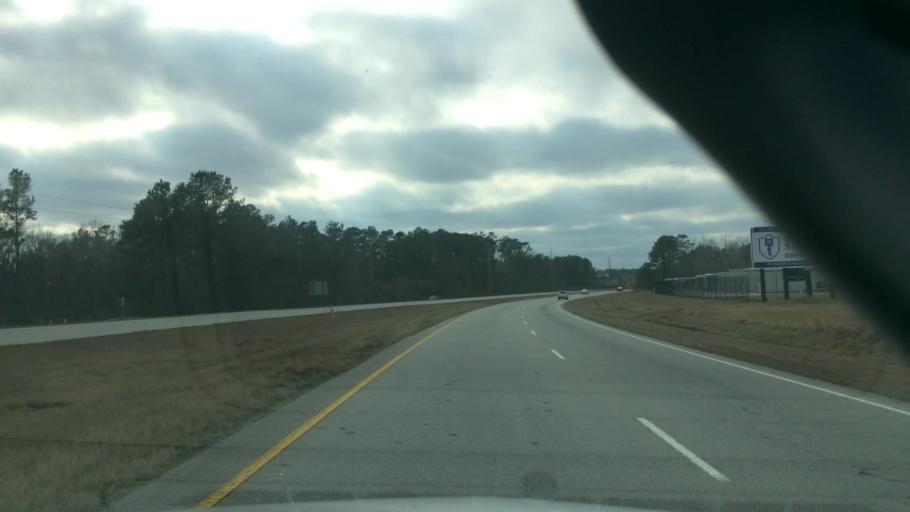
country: US
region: North Carolina
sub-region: Brunswick County
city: Shallotte
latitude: 33.9598
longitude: -78.4200
